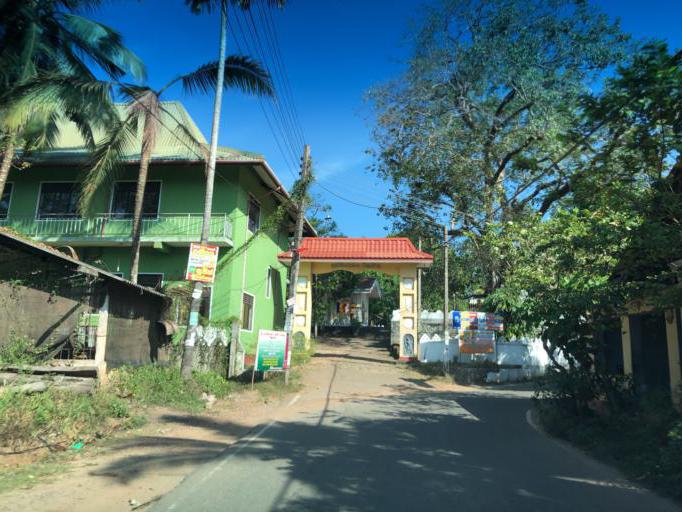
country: LK
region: Western
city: Homagama
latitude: 6.7852
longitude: 79.9782
